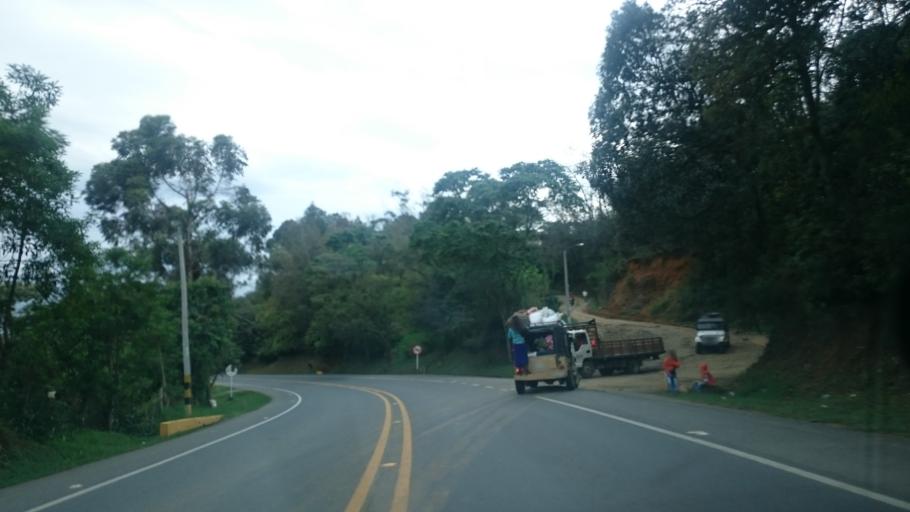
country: CO
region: Cauca
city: Cajibio
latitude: 2.6140
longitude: -76.5162
